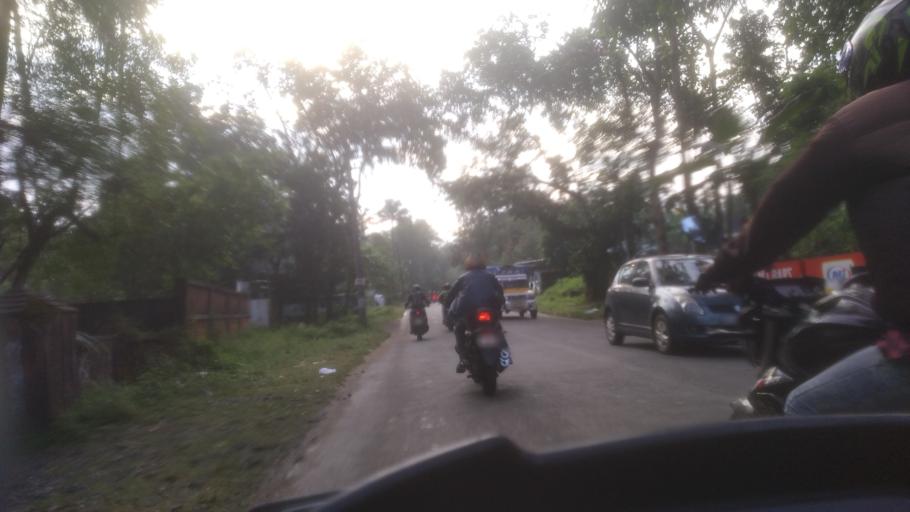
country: IN
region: Kerala
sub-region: Ernakulam
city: Perumpavur
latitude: 10.1041
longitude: 76.5392
